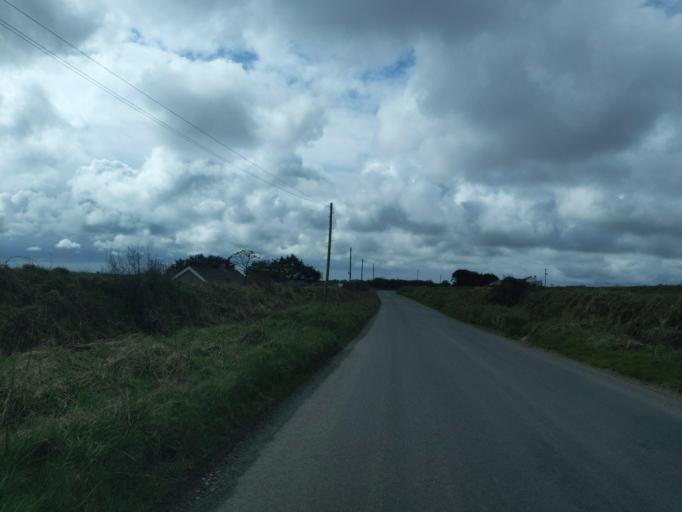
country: GB
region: England
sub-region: Cornwall
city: Camelford
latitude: 50.6409
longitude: -4.6456
